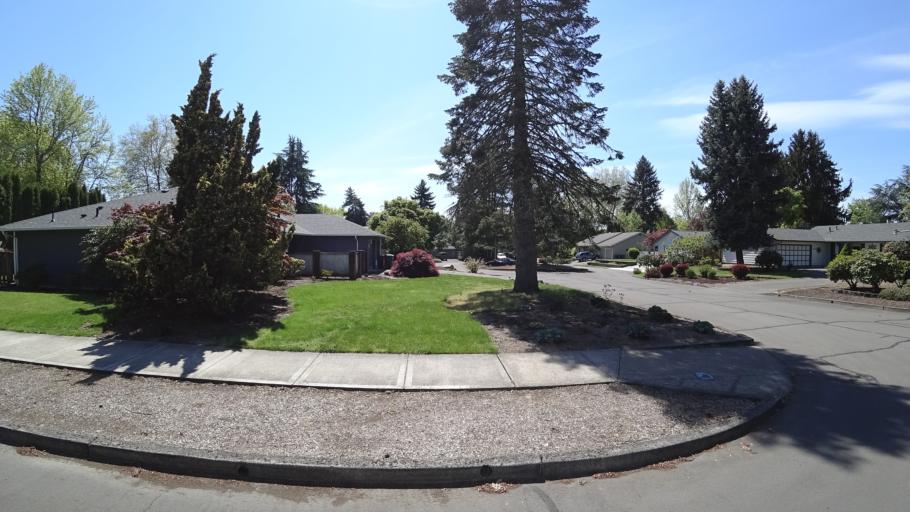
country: US
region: Oregon
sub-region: Washington County
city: Hillsboro
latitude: 45.5020
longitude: -122.9591
